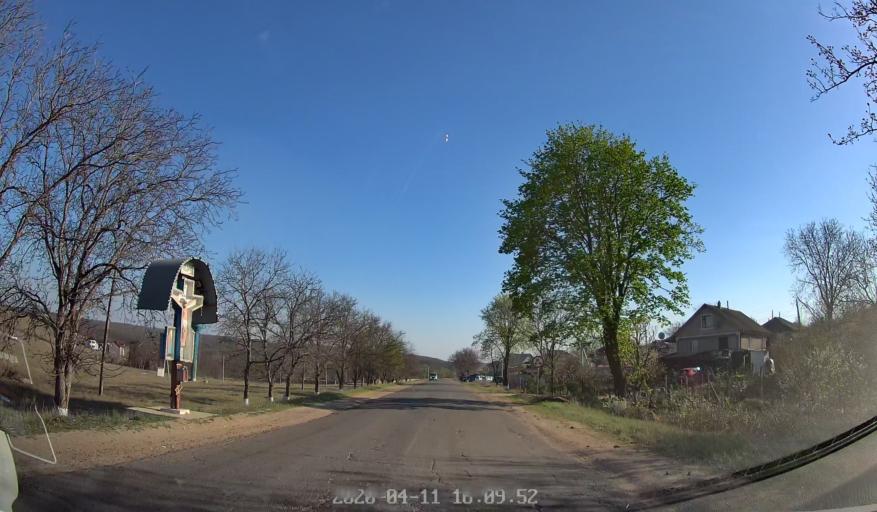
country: MD
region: Chisinau
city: Vadul lui Voda
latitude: 47.0711
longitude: 29.1365
